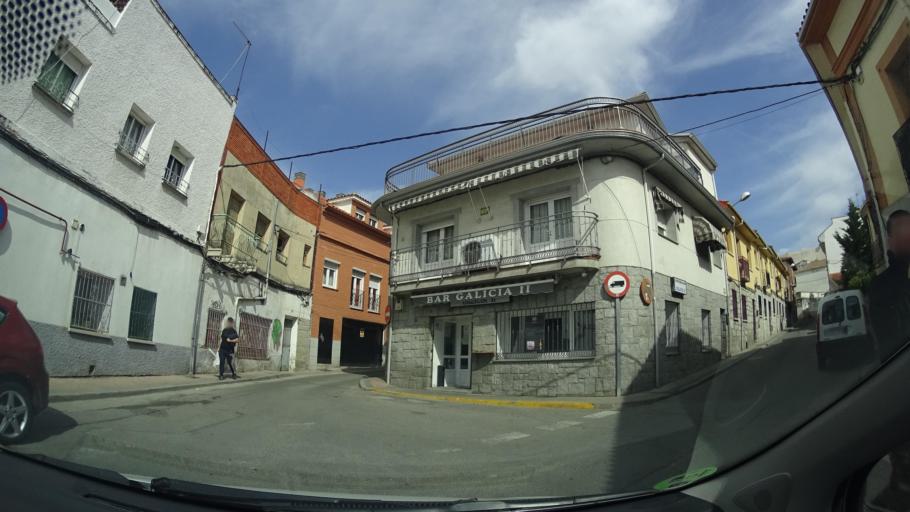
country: ES
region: Madrid
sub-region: Provincia de Madrid
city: Colmenar Viejo
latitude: 40.6566
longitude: -3.7674
